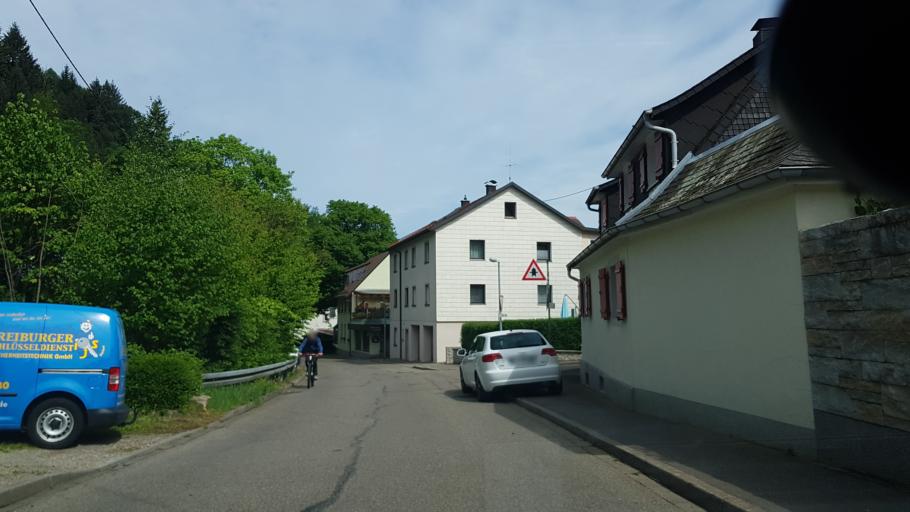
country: DE
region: Baden-Wuerttemberg
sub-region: Freiburg Region
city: Kirchzarten
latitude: 47.9633
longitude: 7.9091
